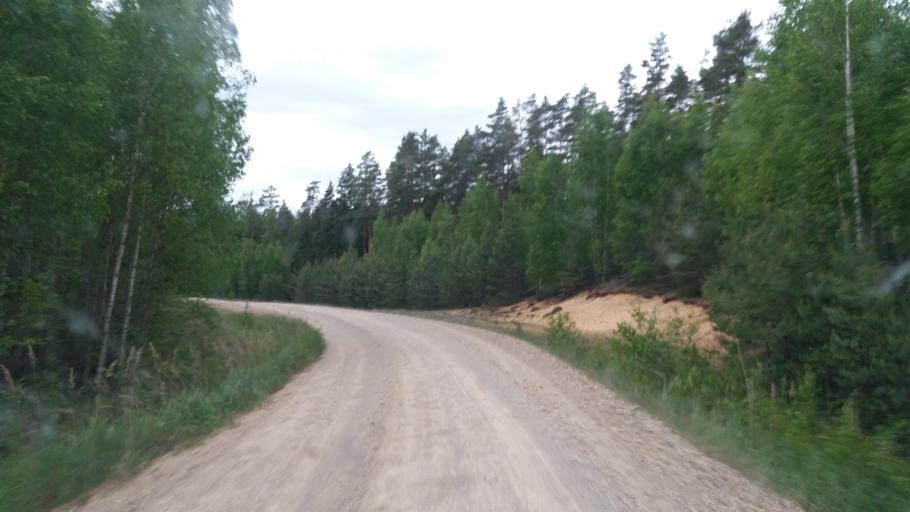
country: LV
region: Kuldigas Rajons
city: Kuldiga
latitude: 57.1531
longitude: 22.1233
